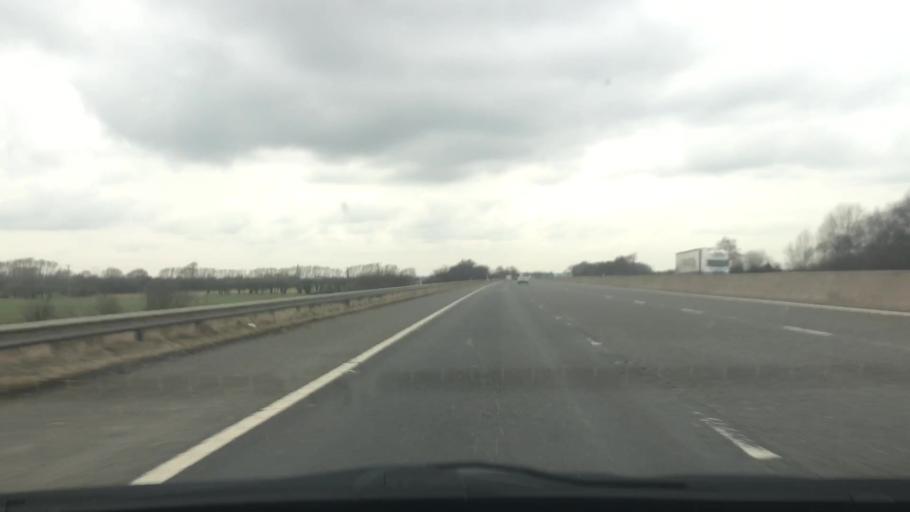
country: GB
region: England
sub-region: North Lincolnshire
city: Crowle
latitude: 53.5724
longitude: -0.8985
